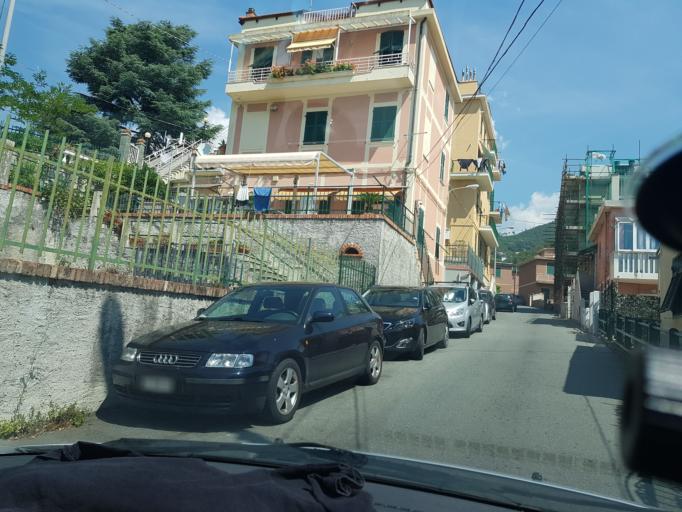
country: IT
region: Liguria
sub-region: Provincia di Genova
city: San Teodoro
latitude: 44.4322
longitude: 8.8418
